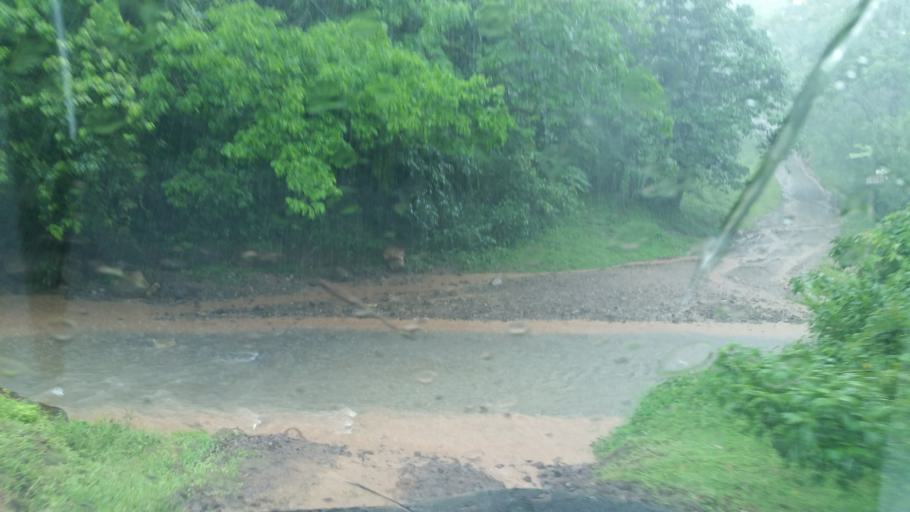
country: NI
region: Atlantico Norte (RAAN)
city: Waslala
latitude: 13.1552
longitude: -85.4301
